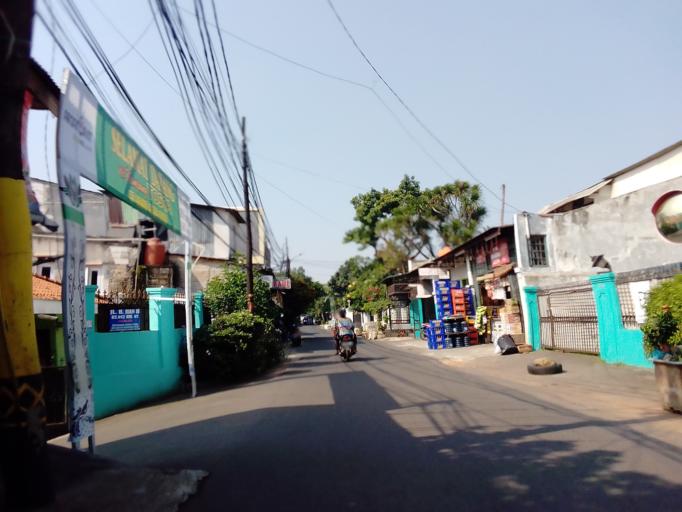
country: ID
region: Jakarta Raya
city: Jakarta
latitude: -6.2637
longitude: 106.8042
